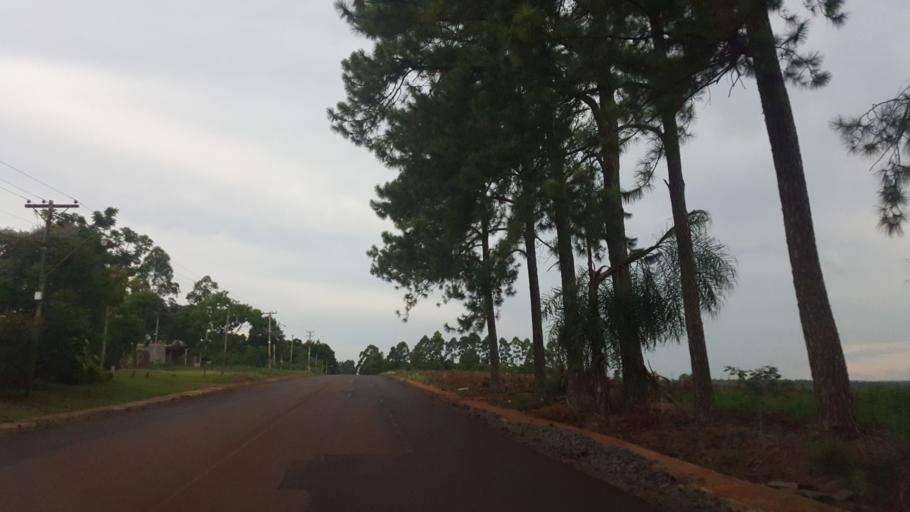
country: AR
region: Misiones
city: Puerto Leoni
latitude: -27.0019
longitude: -55.1641
